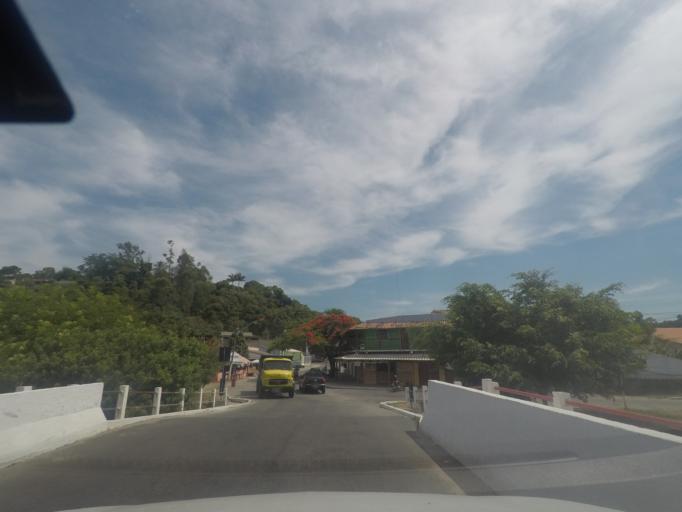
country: BR
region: Rio de Janeiro
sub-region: Marica
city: Marica
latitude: -22.9447
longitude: -42.7517
